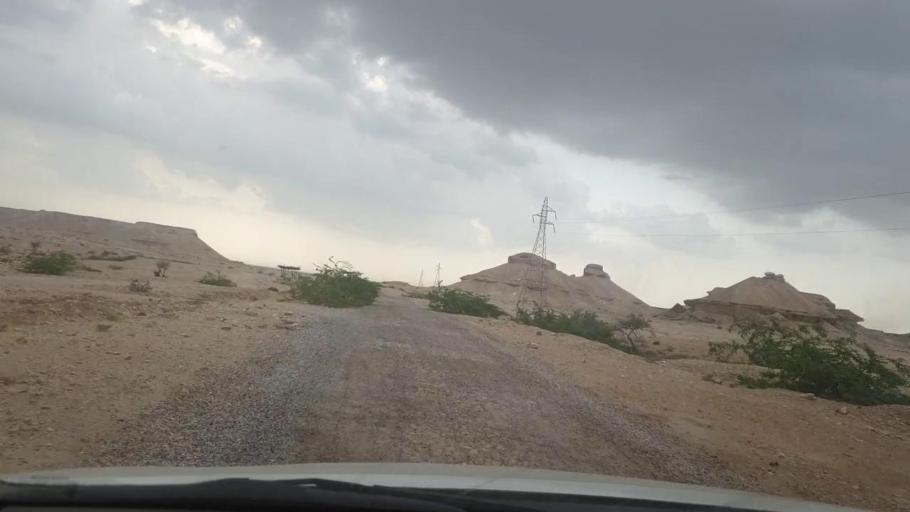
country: PK
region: Sindh
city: Khairpur
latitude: 27.4704
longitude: 68.8956
